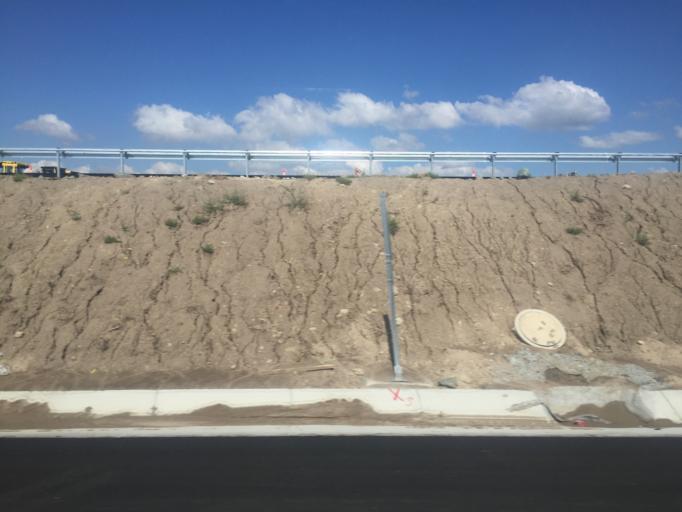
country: TR
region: Balikesir
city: Gobel
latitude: 40.0404
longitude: 28.2196
